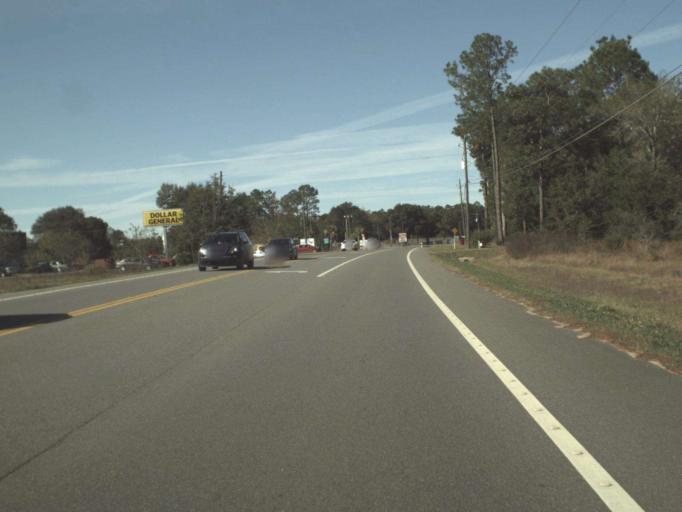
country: US
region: Florida
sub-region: Okaloosa County
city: Crestview
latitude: 30.7656
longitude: -86.6681
